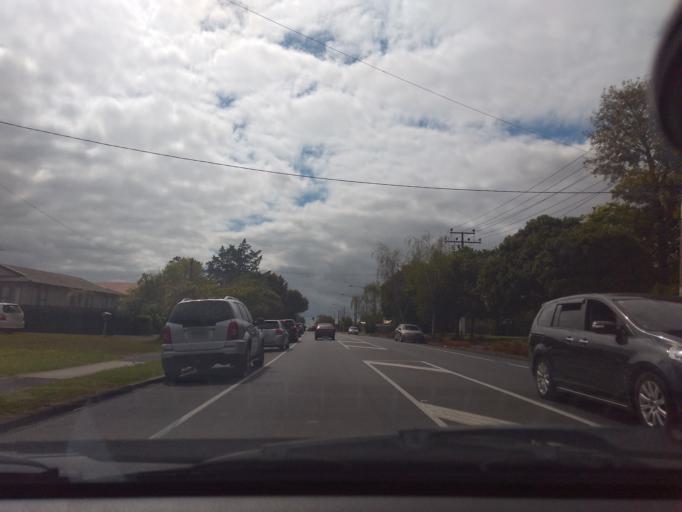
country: NZ
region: Auckland
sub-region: Auckland
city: Rosebank
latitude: -36.8642
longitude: 174.5991
